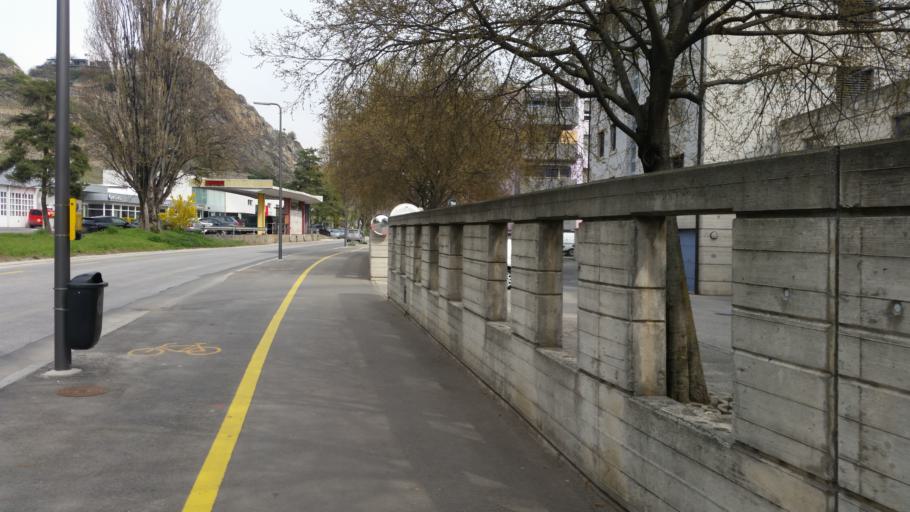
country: CH
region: Valais
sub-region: Sion District
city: Sitten
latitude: 46.2267
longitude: 7.3378
